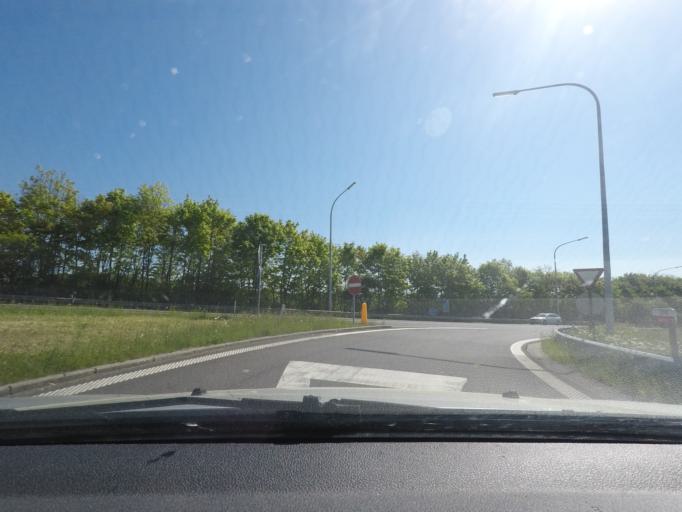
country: BE
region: Wallonia
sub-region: Province de Namur
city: Houyet
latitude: 50.1693
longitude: 5.0710
